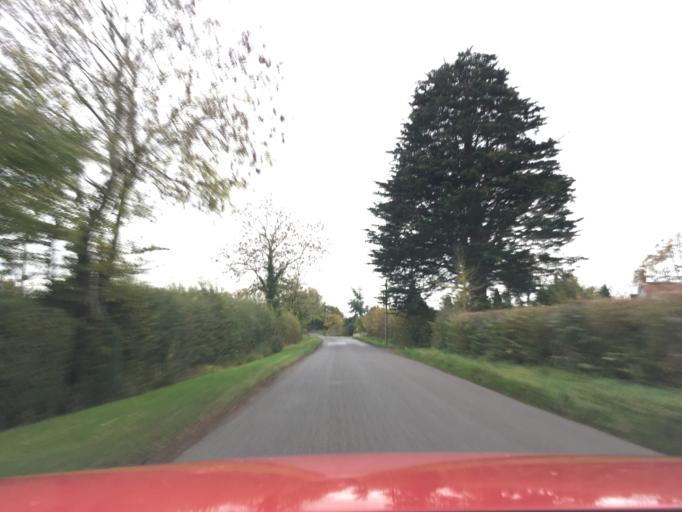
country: GB
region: England
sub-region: Somerset
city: Yeovil
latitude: 51.0093
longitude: -2.5977
